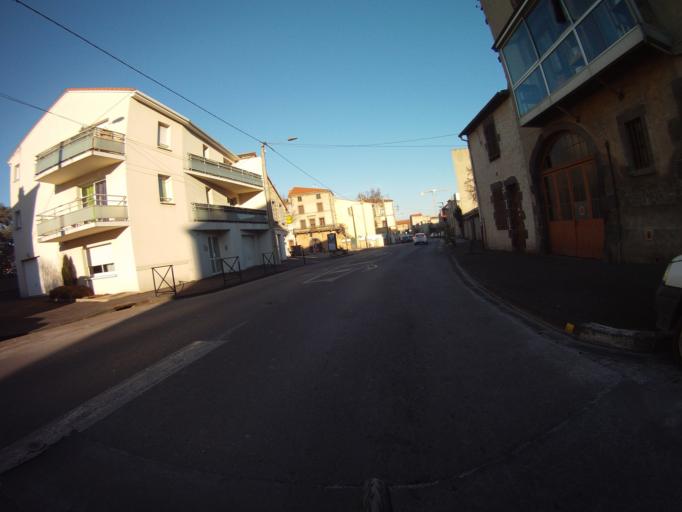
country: FR
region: Auvergne
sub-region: Departement du Puy-de-Dome
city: Aubiere
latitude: 45.7526
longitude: 3.1109
